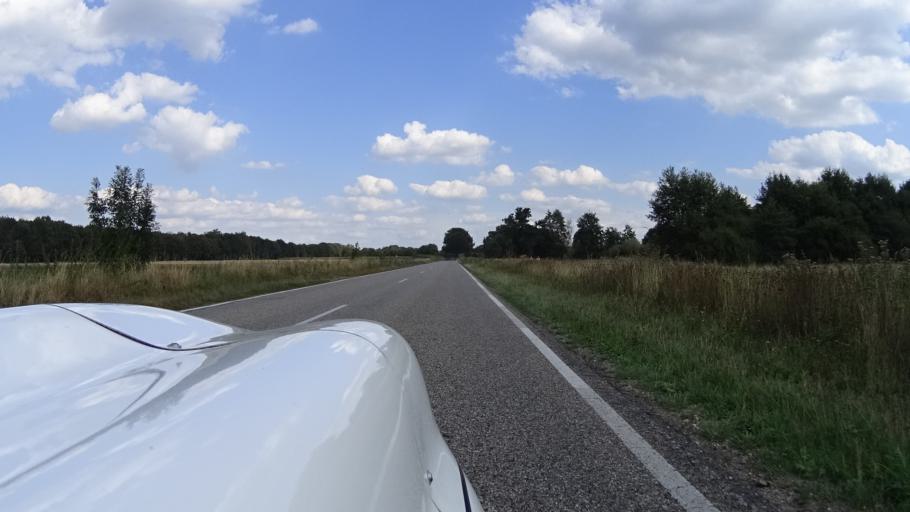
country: NL
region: North Brabant
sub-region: Gemeente Sint Anthonis
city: Sint Anthonis
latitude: 51.6355
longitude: 5.8352
